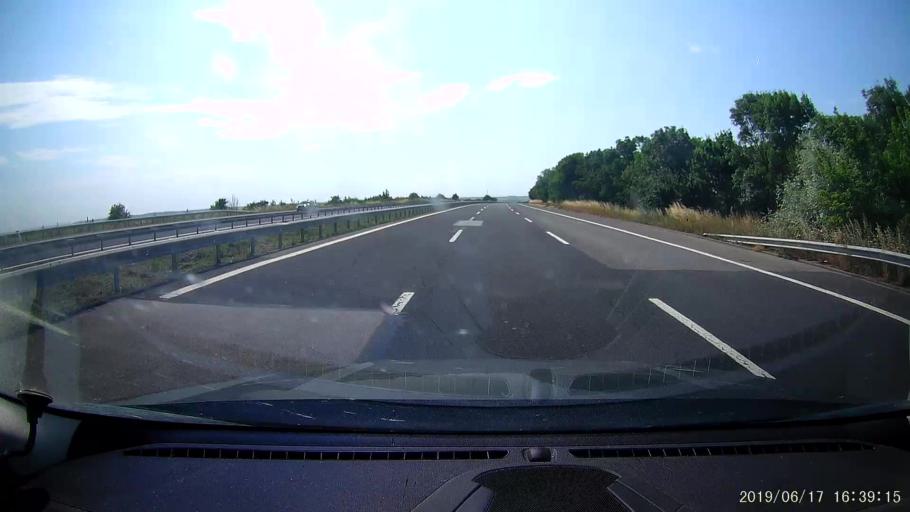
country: TR
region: Kirklareli
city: Luleburgaz
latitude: 41.4476
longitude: 27.4169
